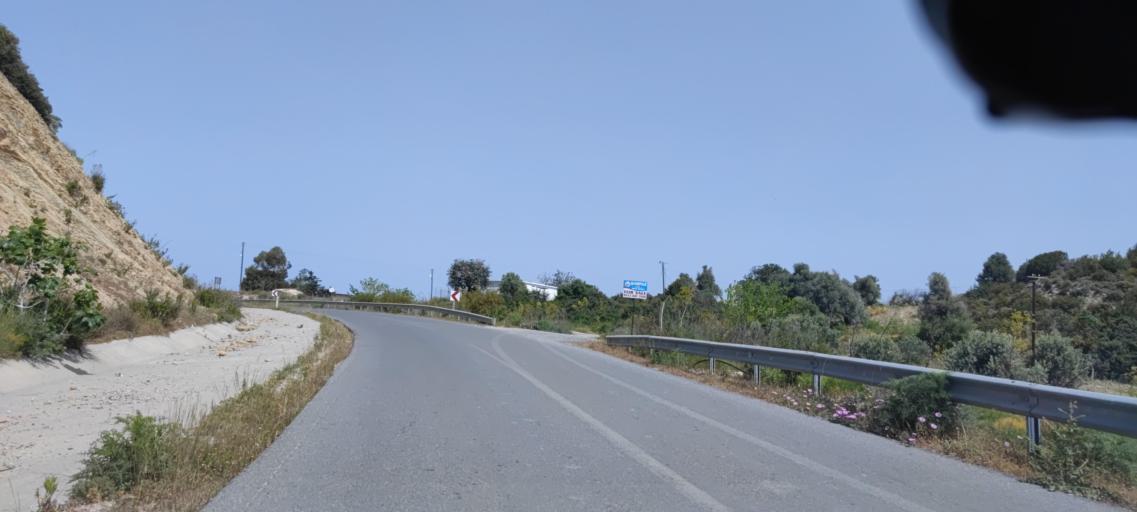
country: CY
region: Ammochostos
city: Rizokarpaso
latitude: 35.5901
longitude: 34.3919
